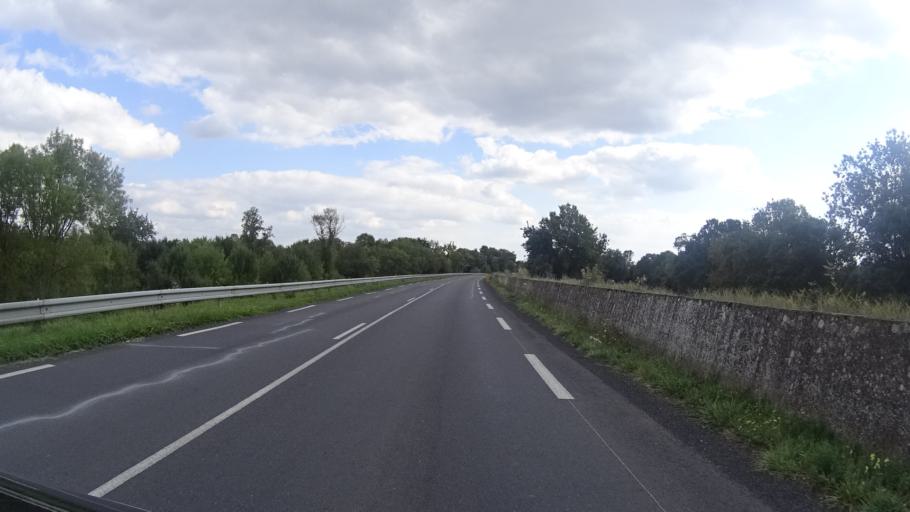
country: FR
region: Pays de la Loire
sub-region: Departement de Maine-et-Loire
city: Les Rosiers-sur-Loire
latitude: 47.3433
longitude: -0.2079
